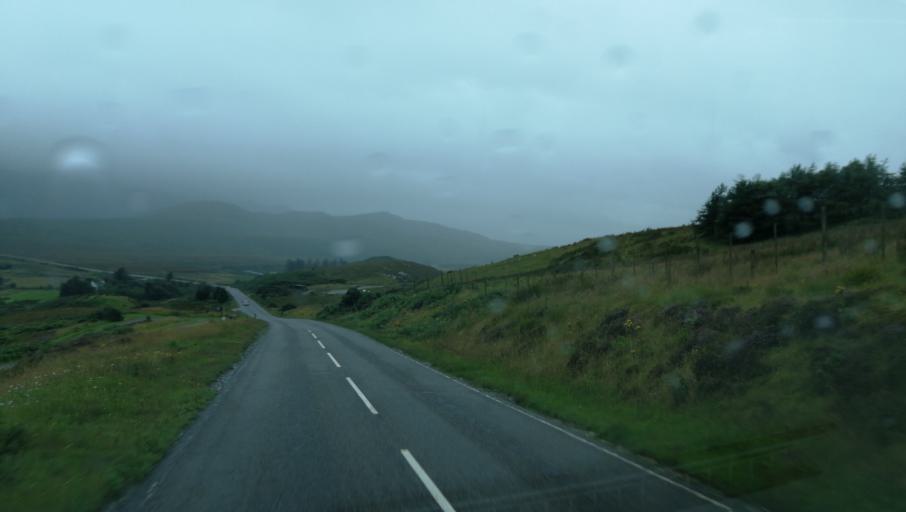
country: GB
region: Scotland
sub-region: Highland
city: Ullapool
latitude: 57.9671
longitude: -5.1306
